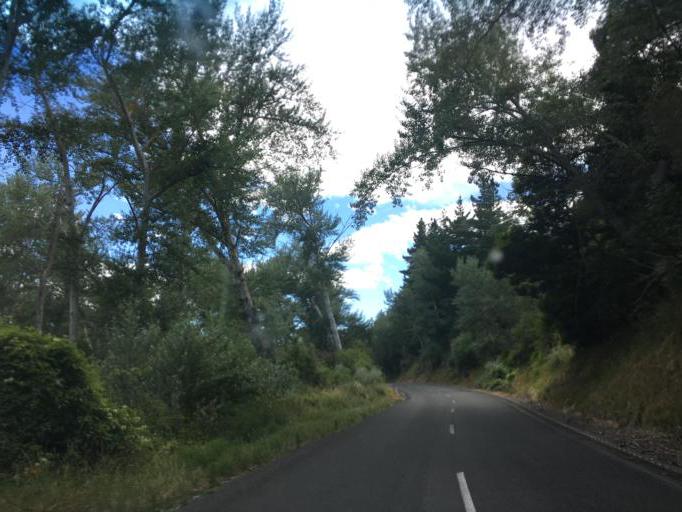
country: NZ
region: Hawke's Bay
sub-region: Hastings District
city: Hastings
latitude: -39.7341
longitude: 176.9054
